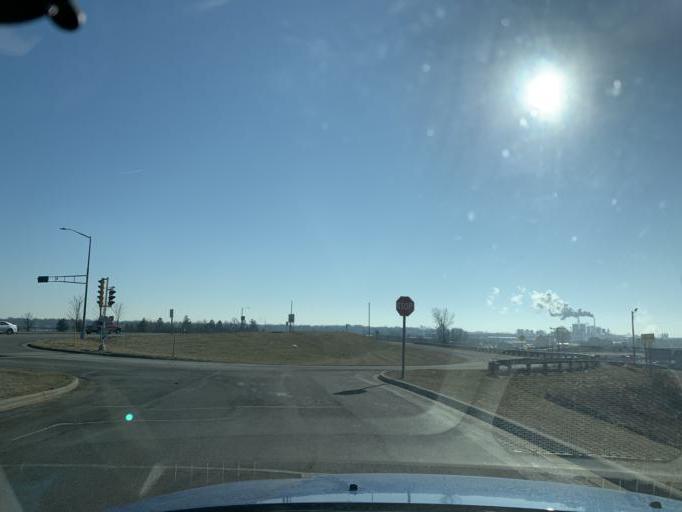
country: US
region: Wisconsin
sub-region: Green County
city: Monroe
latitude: 42.6078
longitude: -89.6667
